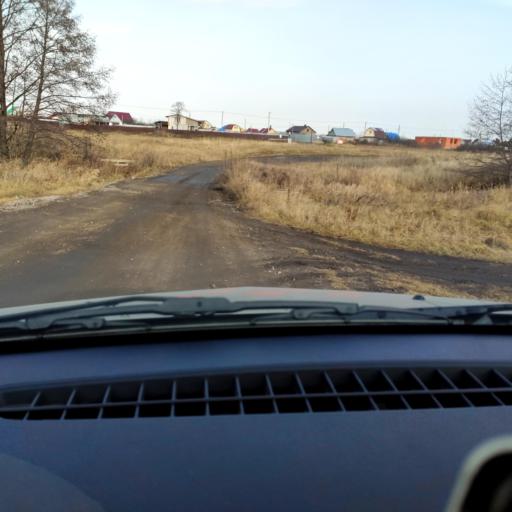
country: RU
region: Bashkortostan
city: Avdon
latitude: 54.4932
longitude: 55.8549
